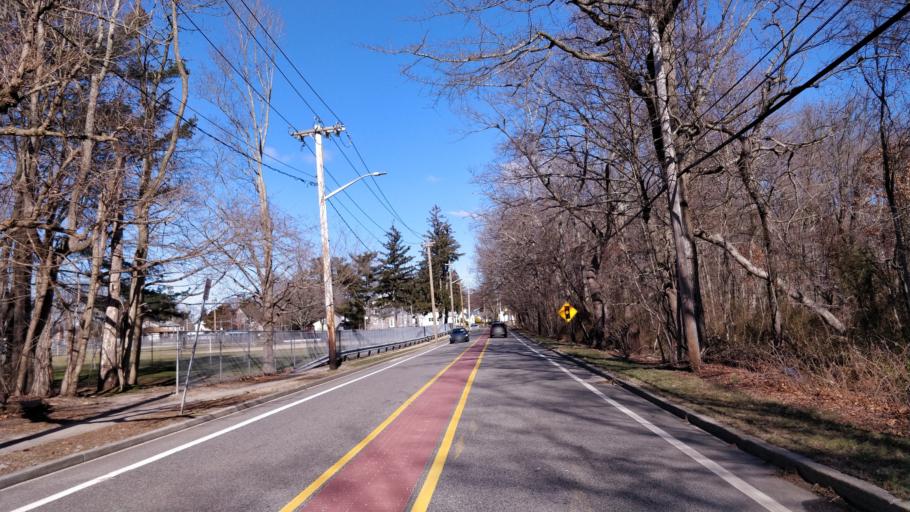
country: US
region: New York
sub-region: Suffolk County
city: Smithtown
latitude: 40.8457
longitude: -73.1970
